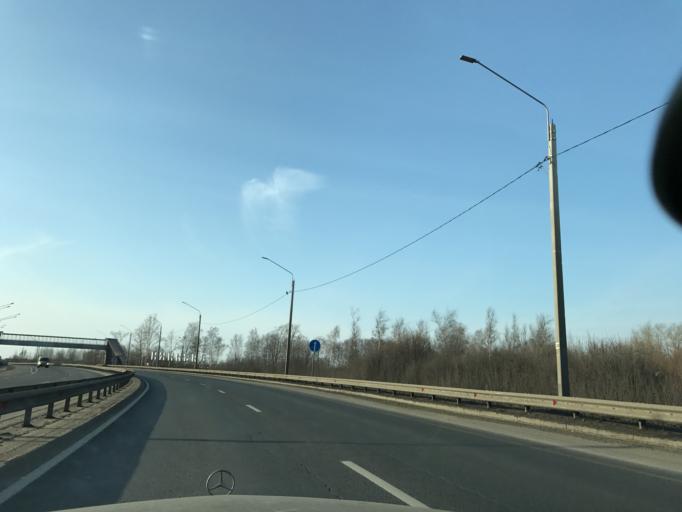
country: RU
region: Vladimir
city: Vyazniki
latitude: 56.2390
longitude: 42.1060
